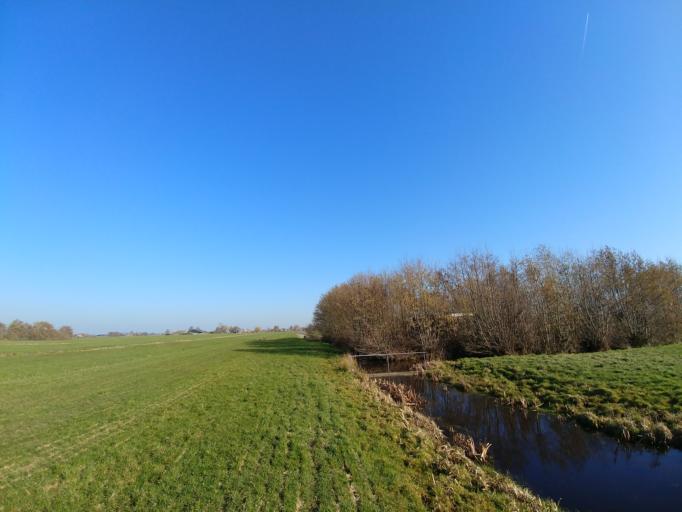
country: NL
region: Utrecht
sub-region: Gemeente Woerden
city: Woerden
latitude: 52.1475
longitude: 4.8835
